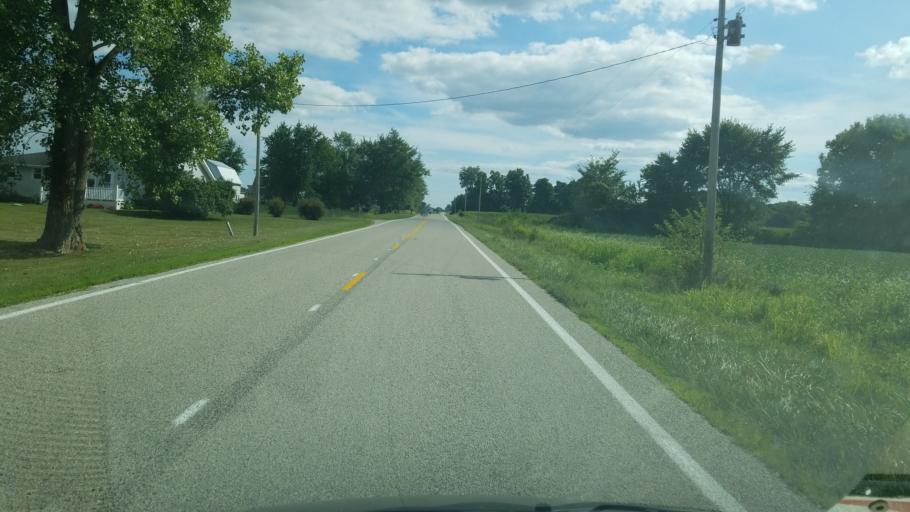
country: US
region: Ohio
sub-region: Logan County
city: De Graff
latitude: 40.2295
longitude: -83.9399
